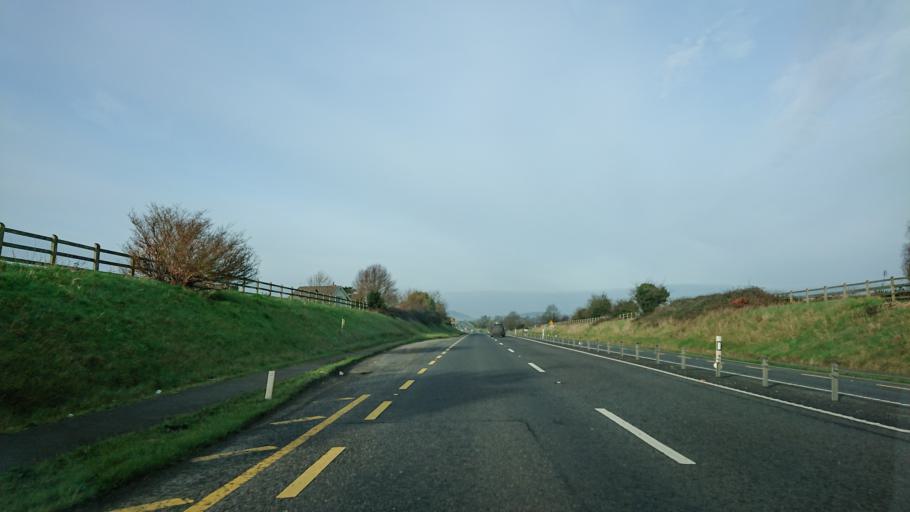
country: IE
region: Munster
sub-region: Waterford
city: Portlaw
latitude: 52.3152
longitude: -7.2934
